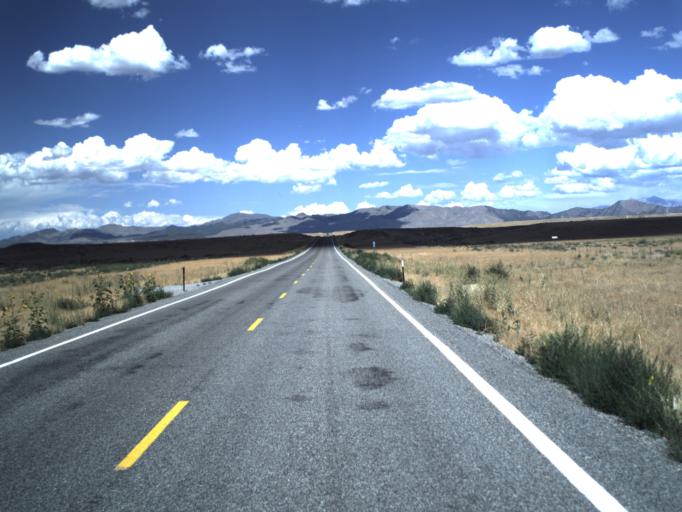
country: US
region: Utah
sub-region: Juab County
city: Nephi
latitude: 39.6793
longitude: -112.2538
